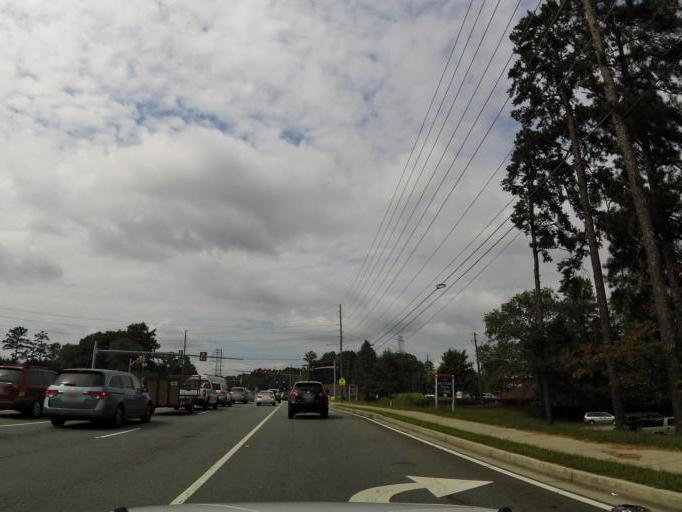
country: US
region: Georgia
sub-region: Cobb County
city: Kennesaw
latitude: 33.9914
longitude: -84.6280
